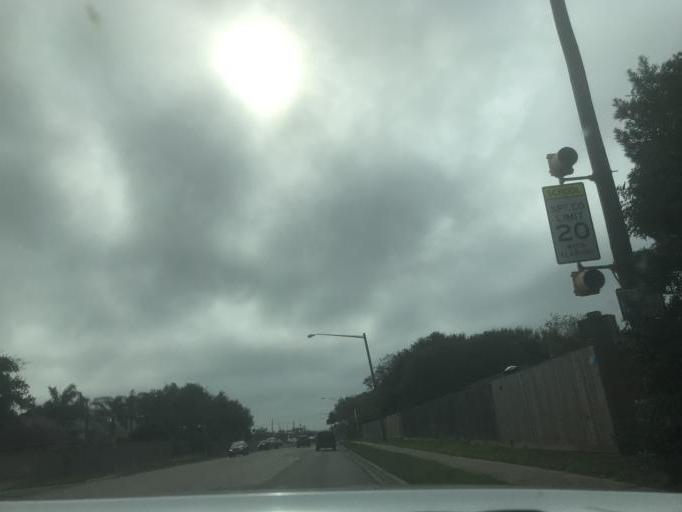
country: US
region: Texas
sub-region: Nueces County
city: Corpus Christi
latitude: 27.6830
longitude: -97.3669
